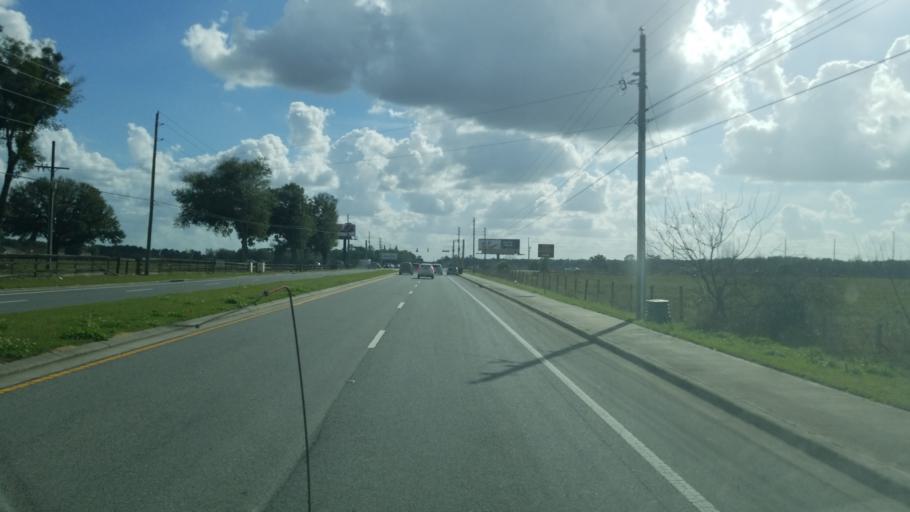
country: US
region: Florida
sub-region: Marion County
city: Ocala
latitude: 29.1521
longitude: -82.2188
